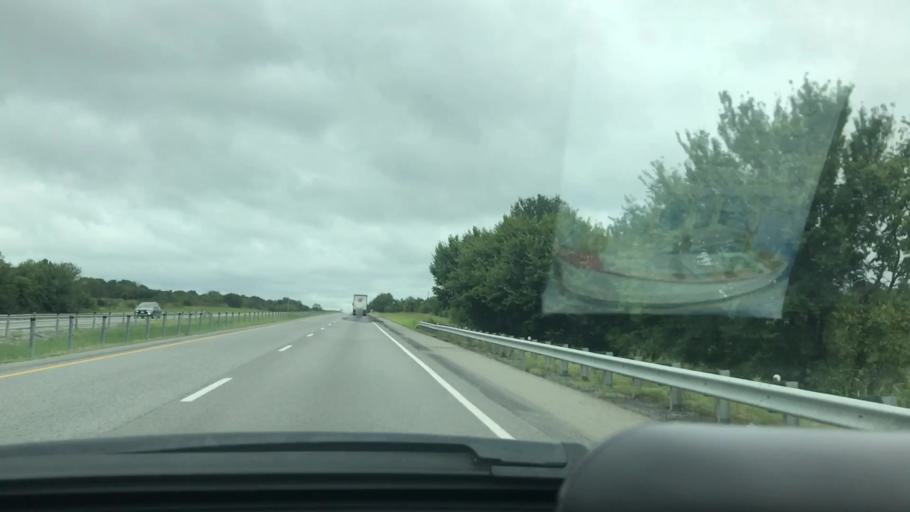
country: US
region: Oklahoma
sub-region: Pittsburg County
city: McAlester
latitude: 34.7957
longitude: -95.8718
